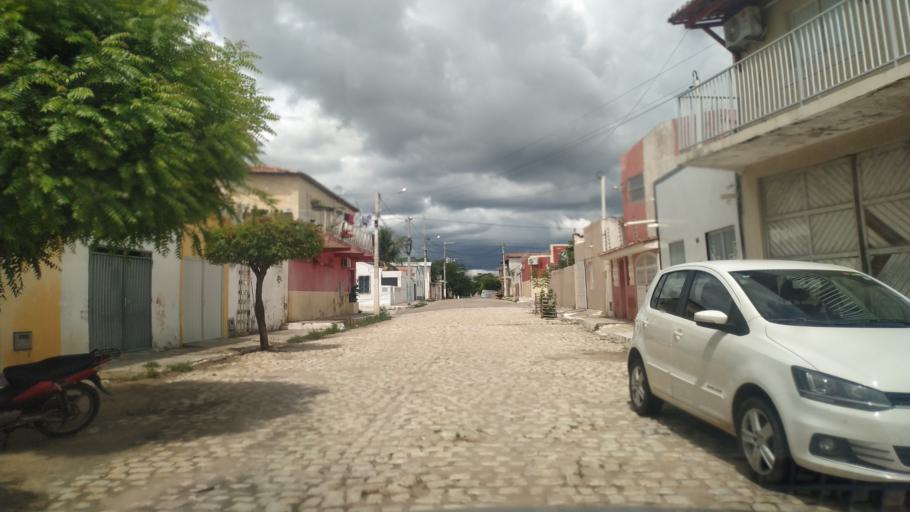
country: BR
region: Rio Grande do Norte
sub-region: Areia Branca
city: Areia Branca
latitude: -4.9516
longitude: -37.1350
